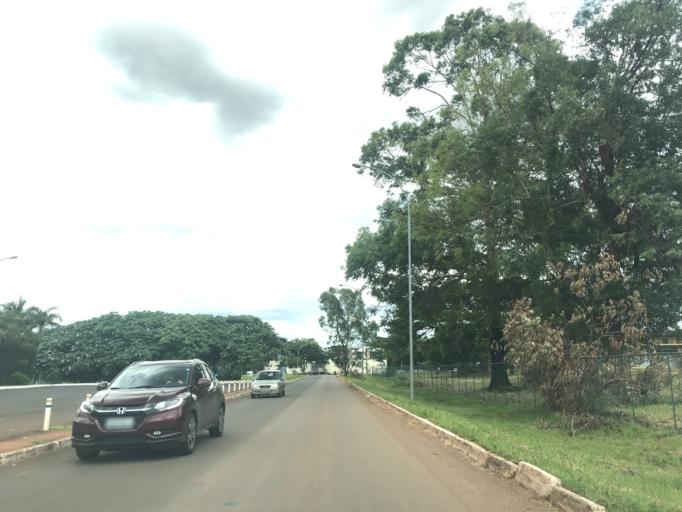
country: BR
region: Federal District
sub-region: Brasilia
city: Brasilia
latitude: -15.8338
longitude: -47.9095
